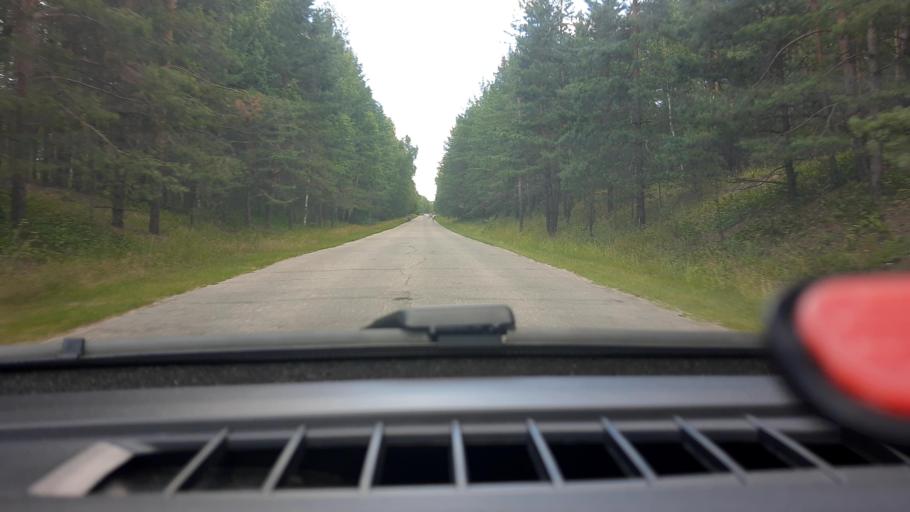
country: RU
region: Nizjnij Novgorod
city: Babino
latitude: 56.3255
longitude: 43.6342
